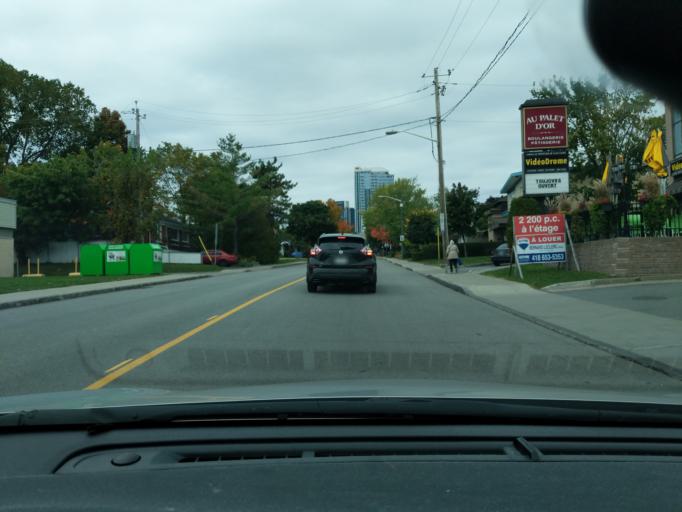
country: CA
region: Quebec
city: L'Ancienne-Lorette
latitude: 46.7631
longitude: -71.2828
